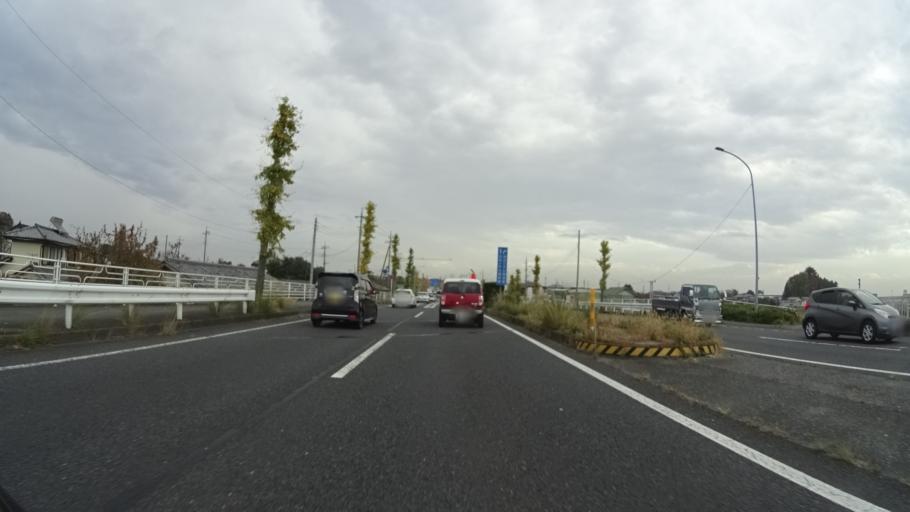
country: JP
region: Gunma
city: Isesaki
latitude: 36.3695
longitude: 139.1479
